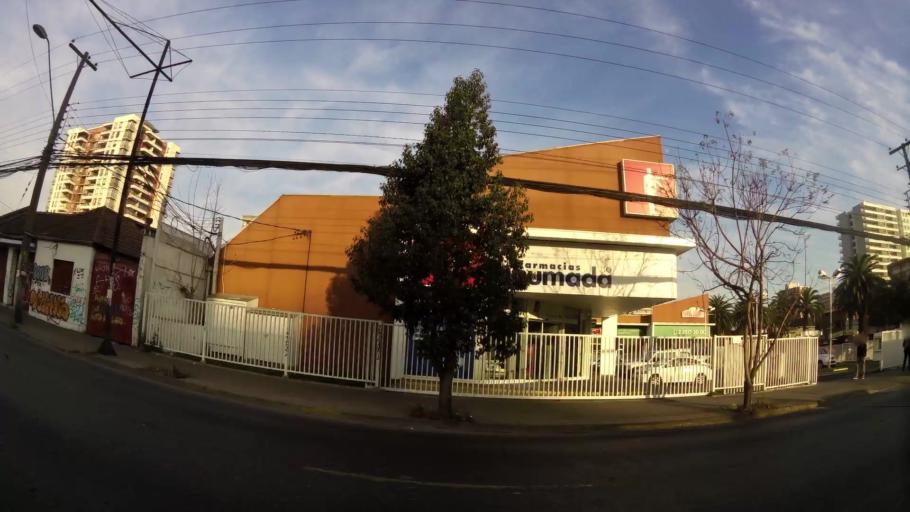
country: CL
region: Santiago Metropolitan
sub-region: Provincia de Santiago
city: Santiago
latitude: -33.4998
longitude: -70.6540
